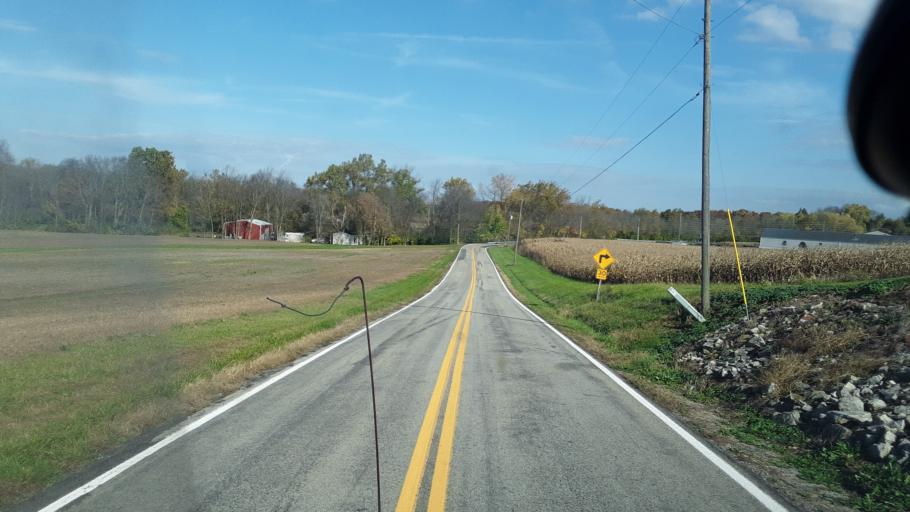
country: US
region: Ohio
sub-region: Highland County
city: Leesburg
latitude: 39.3432
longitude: -83.5845
